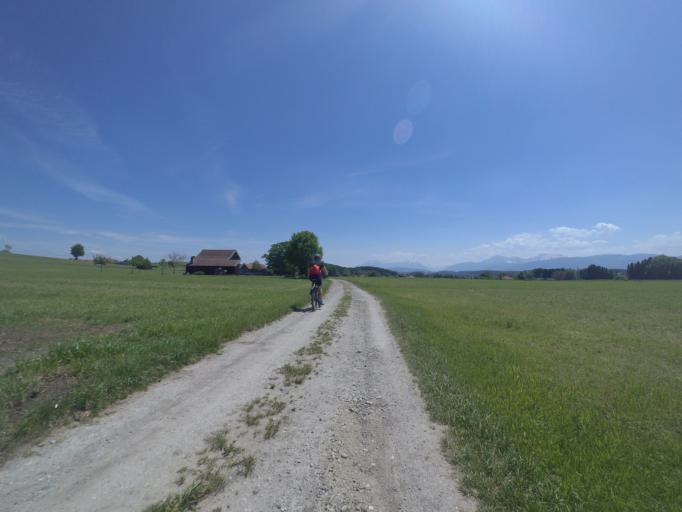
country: DE
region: Bavaria
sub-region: Upper Bavaria
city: Petting
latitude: 47.9382
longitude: 12.7997
